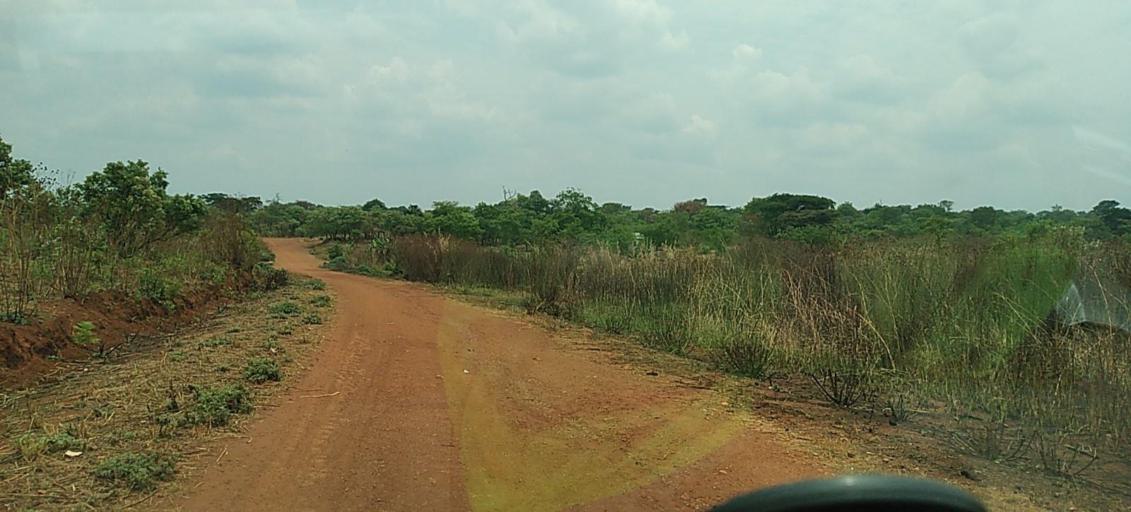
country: ZM
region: North-Western
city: Kansanshi
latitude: -12.0435
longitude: 26.3894
